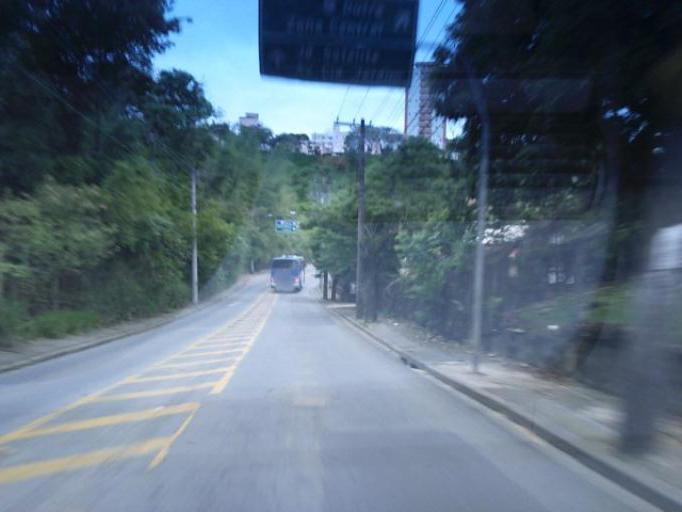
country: BR
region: Sao Paulo
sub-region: Sao Jose Dos Campos
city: Sao Jose dos Campos
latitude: -23.2291
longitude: -45.8759
